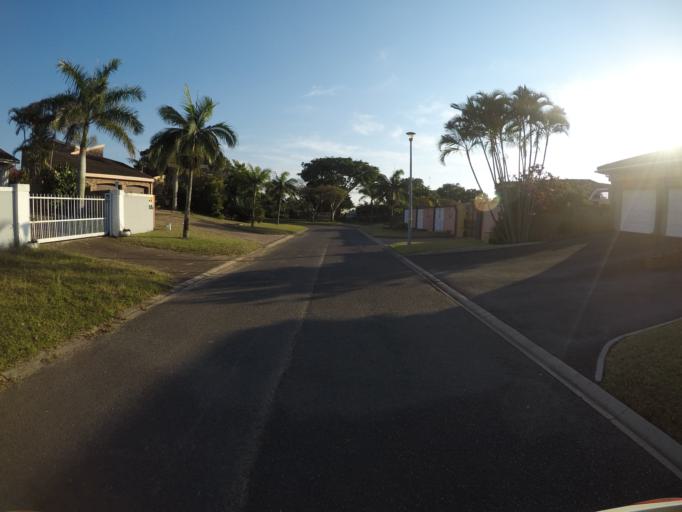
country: ZA
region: KwaZulu-Natal
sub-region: uThungulu District Municipality
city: Richards Bay
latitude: -28.7762
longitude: 32.1145
